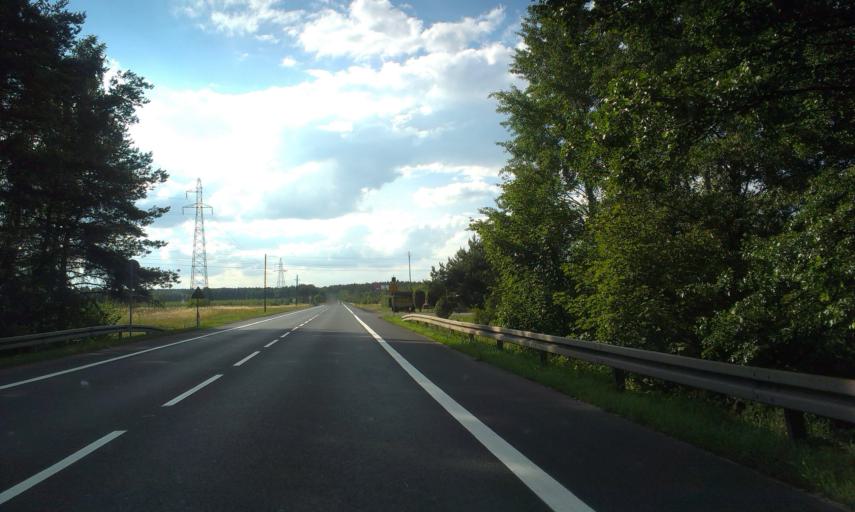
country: PL
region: Greater Poland Voivodeship
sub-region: Powiat pilski
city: Pila
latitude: 53.1831
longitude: 16.7685
